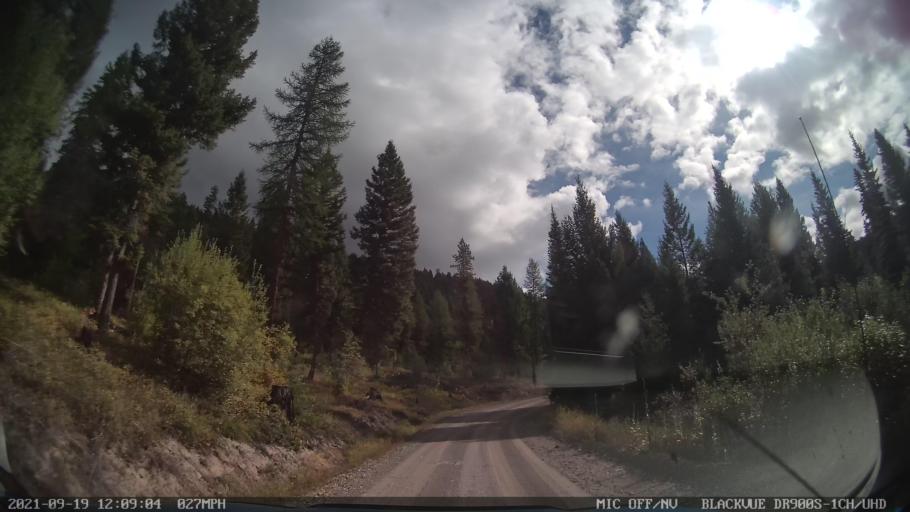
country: US
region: Montana
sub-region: Missoula County
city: Seeley Lake
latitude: 47.1848
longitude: -113.3939
